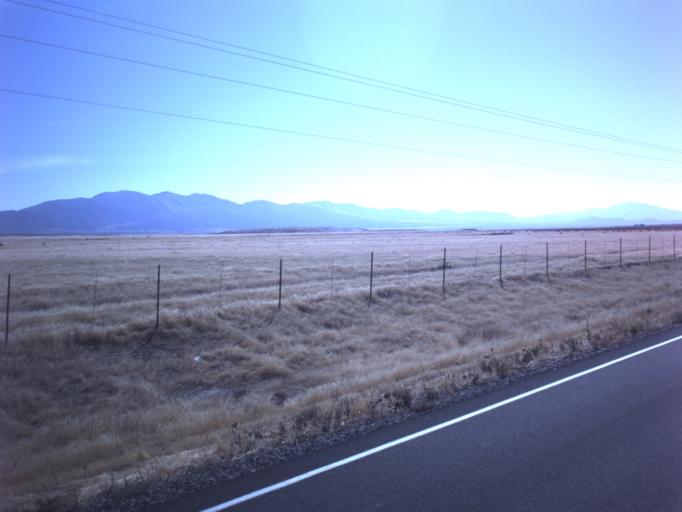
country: US
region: Utah
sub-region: Tooele County
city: Grantsville
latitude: 40.3794
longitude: -112.7468
